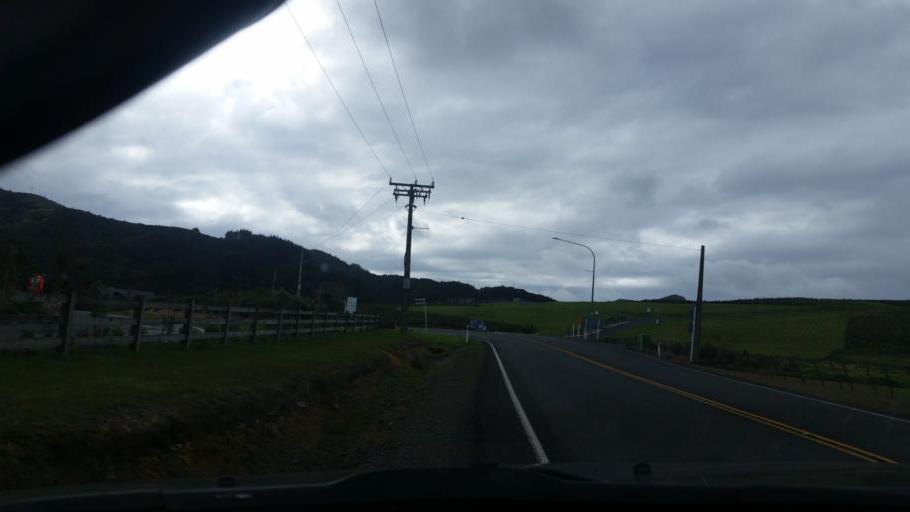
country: NZ
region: Auckland
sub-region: Auckland
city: Wellsford
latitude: -36.0810
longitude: 174.5716
